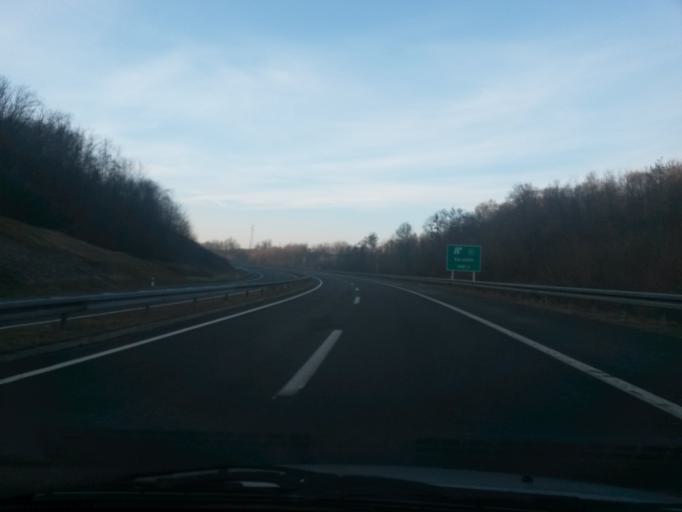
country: HR
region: Varazdinska
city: Jalzabet
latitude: 46.2399
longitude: 16.4100
